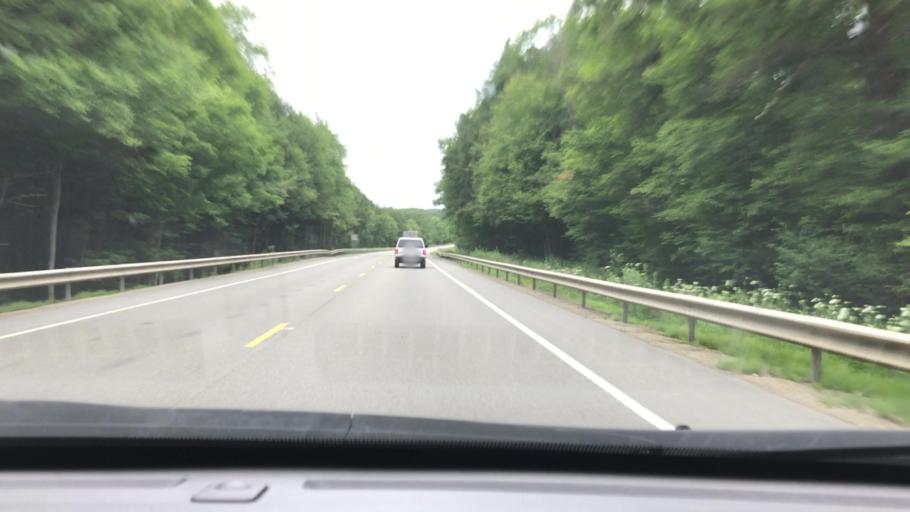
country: US
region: Pennsylvania
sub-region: McKean County
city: Kane
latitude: 41.6836
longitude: -78.6882
